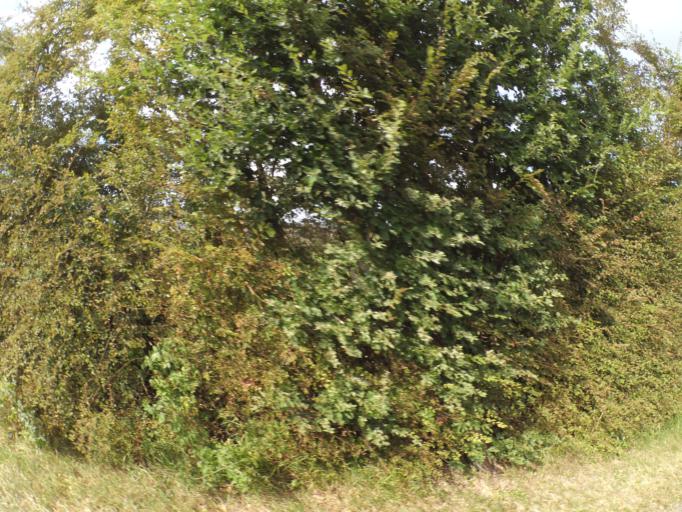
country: FR
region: Pays de la Loire
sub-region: Departement de Maine-et-Loire
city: Saint-Jean
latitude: 47.1892
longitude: -0.3581
